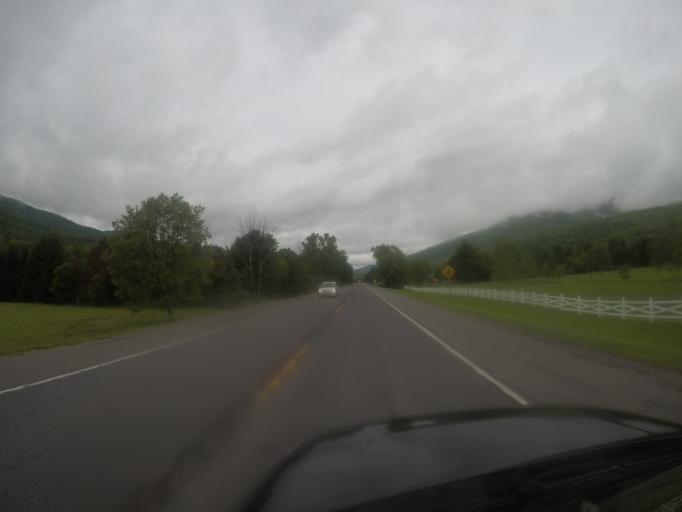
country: US
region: New York
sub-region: Ulster County
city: Shokan
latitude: 42.0460
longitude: -74.2853
